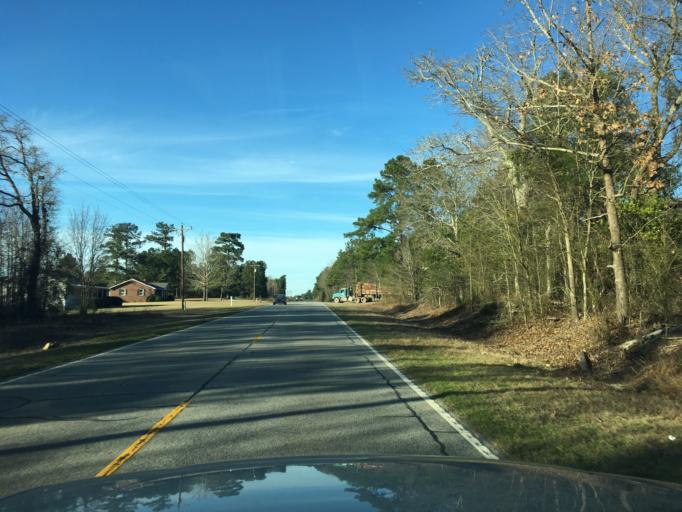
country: US
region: South Carolina
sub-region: Lexington County
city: Batesburg
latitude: 33.7658
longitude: -81.6415
